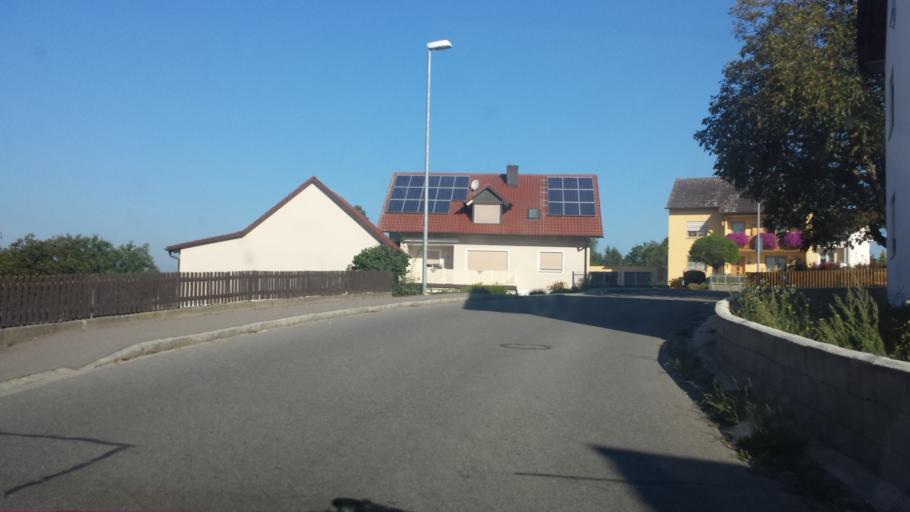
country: DE
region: Bavaria
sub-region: Lower Bavaria
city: Neustadt an der Donau
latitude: 48.8339
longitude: 11.7717
